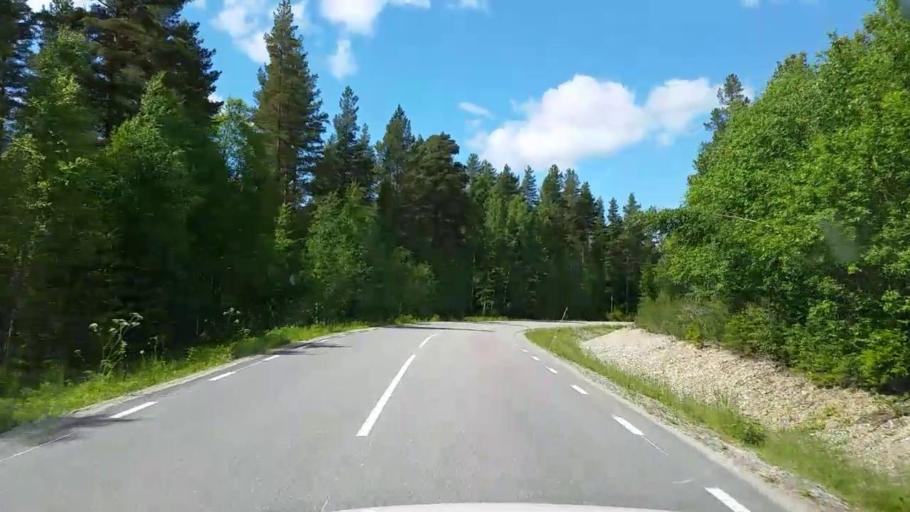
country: SE
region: Gaevleborg
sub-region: Ovanakers Kommun
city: Alfta
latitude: 61.2832
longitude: 16.0970
